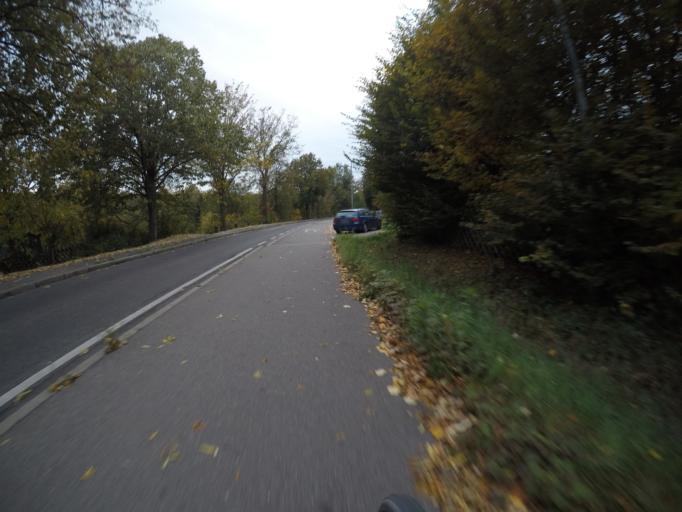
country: DE
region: Baden-Wuerttemberg
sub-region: Regierungsbezirk Stuttgart
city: Leinfelden-Echterdingen
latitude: 48.7358
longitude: 9.1245
